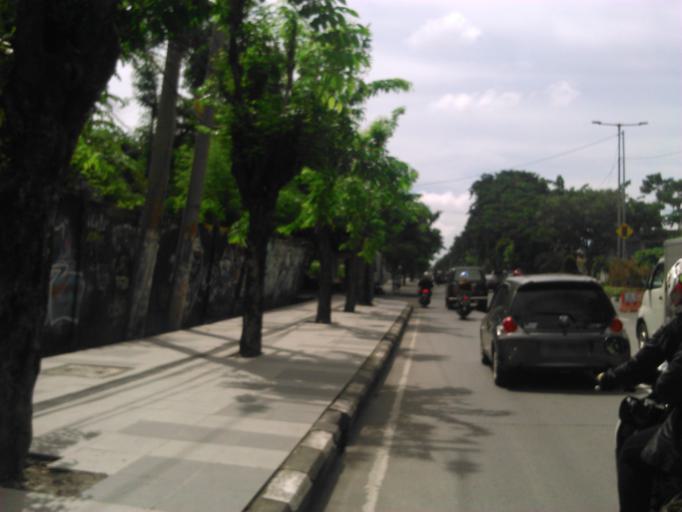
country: ID
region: East Java
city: Jagirsidosermo
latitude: -7.2918
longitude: 112.7200
